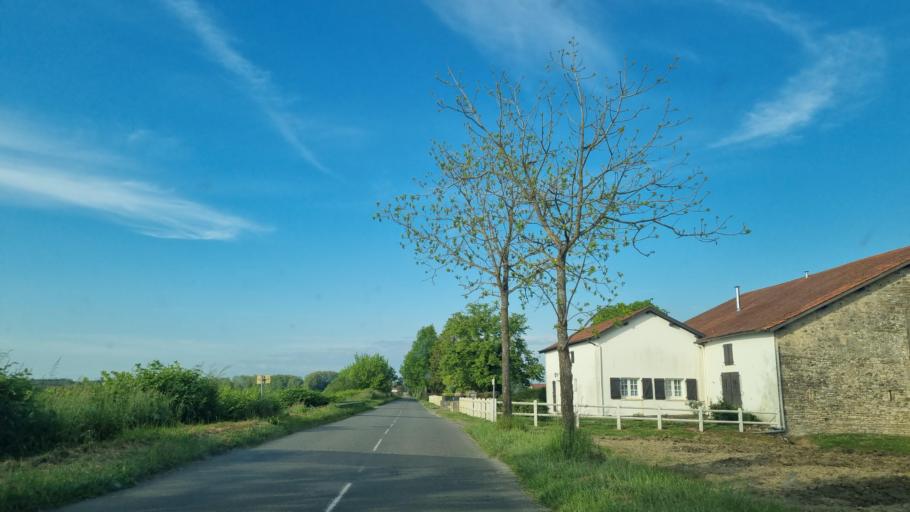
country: FR
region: Aquitaine
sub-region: Departement des Pyrenees-Atlantiques
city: Bardos
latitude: 43.5391
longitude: -1.2030
